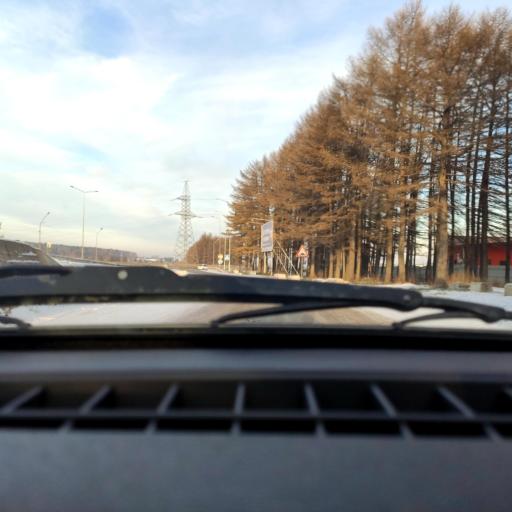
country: RU
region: Bashkortostan
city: Avdon
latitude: 54.6730
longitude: 55.7855
